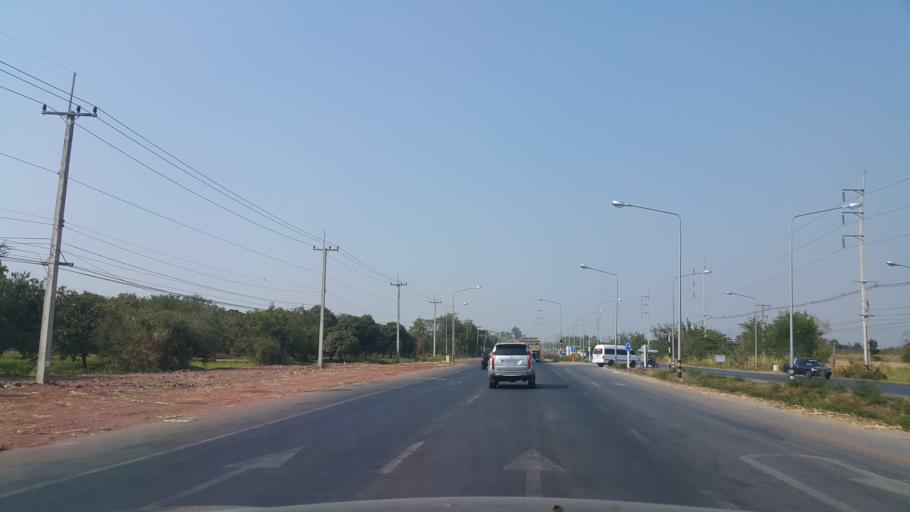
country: TH
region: Chaiyaphum
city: Phu Khiao
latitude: 16.4293
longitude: 102.1288
